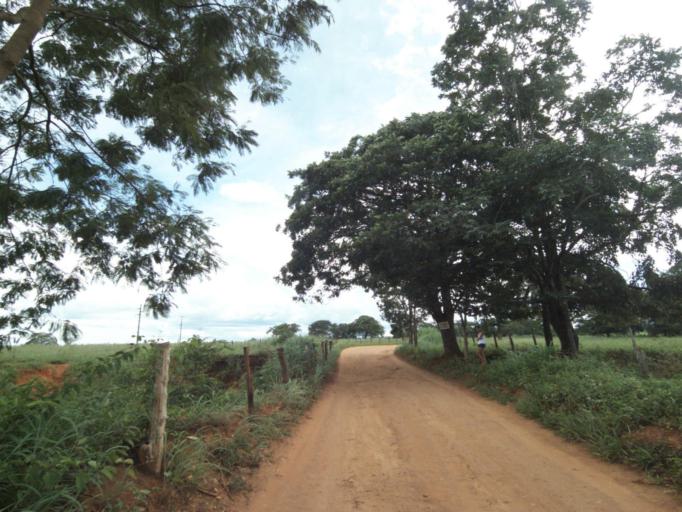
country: BR
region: Goias
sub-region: Jaragua
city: Jaragua
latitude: -15.8363
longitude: -49.2760
